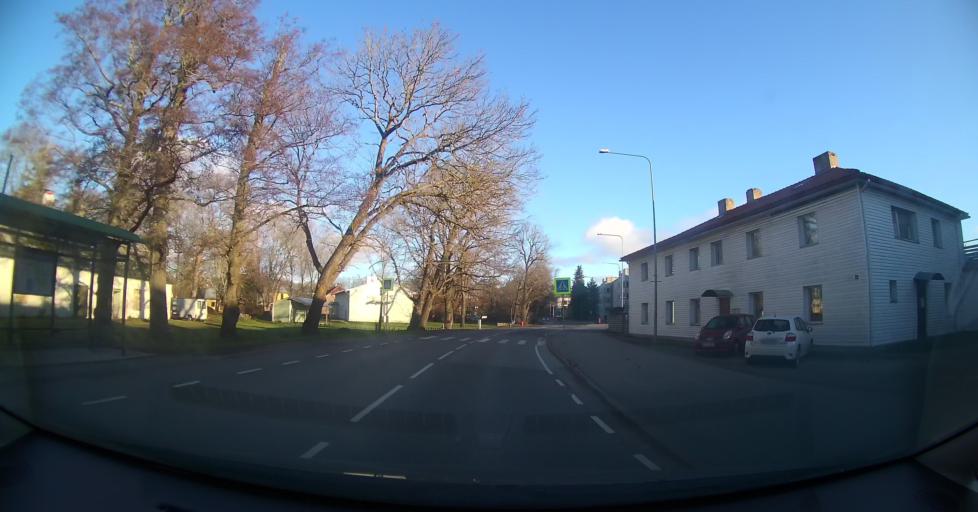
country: EE
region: Harju
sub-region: Viimsi vald
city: Viimsi
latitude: 59.5001
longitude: 24.8343
